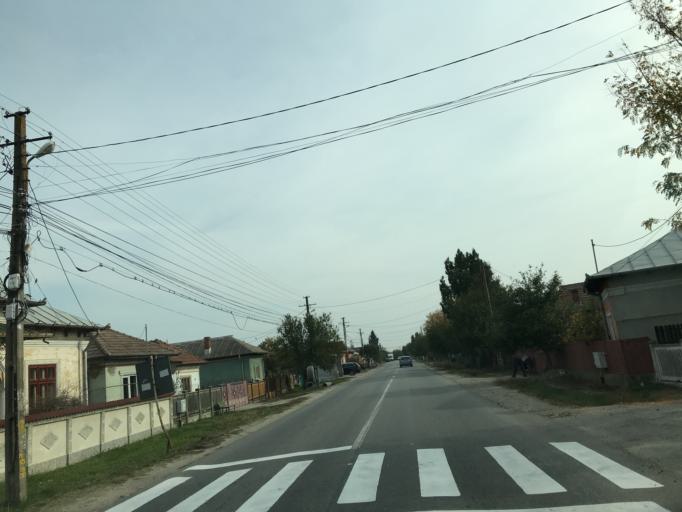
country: RO
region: Olt
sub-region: Comuna Slatioara
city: Slatioara
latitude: 44.4093
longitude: 24.3260
